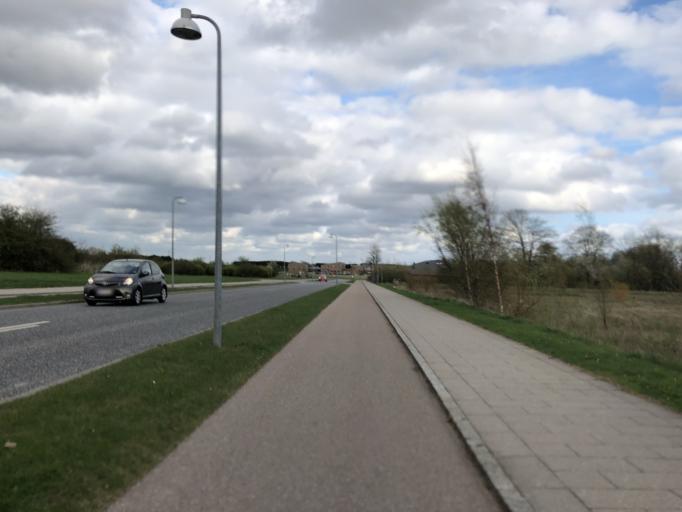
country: DK
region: Zealand
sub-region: Ringsted Kommune
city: Ringsted
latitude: 55.4510
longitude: 11.7966
